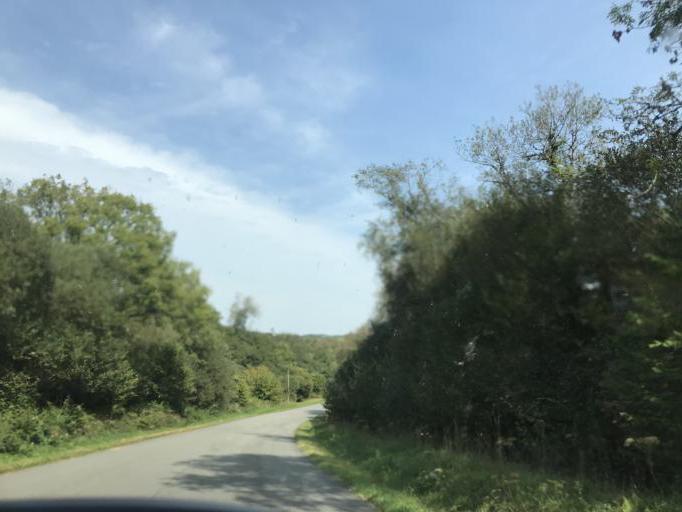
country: FR
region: Brittany
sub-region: Departement du Finistere
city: Loperec
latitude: 48.2957
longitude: -4.0398
